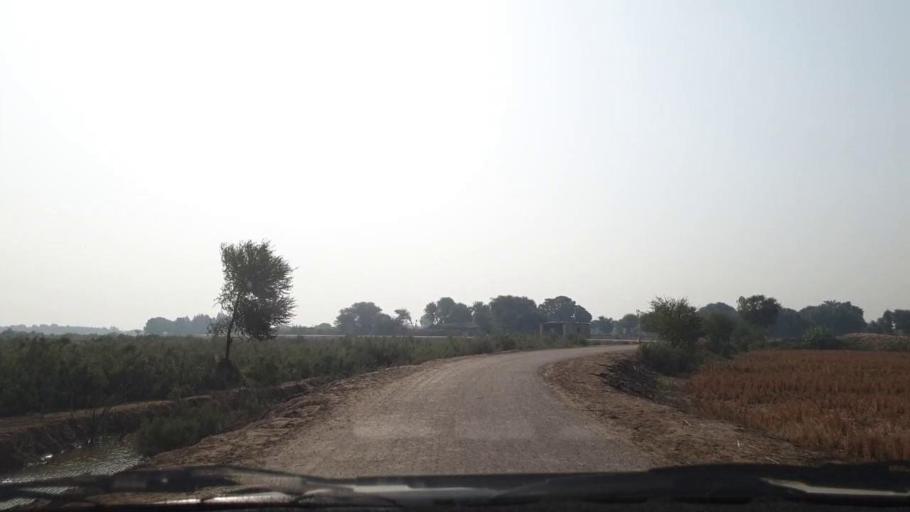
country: PK
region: Sindh
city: Tando Muhammad Khan
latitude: 25.0072
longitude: 68.4505
